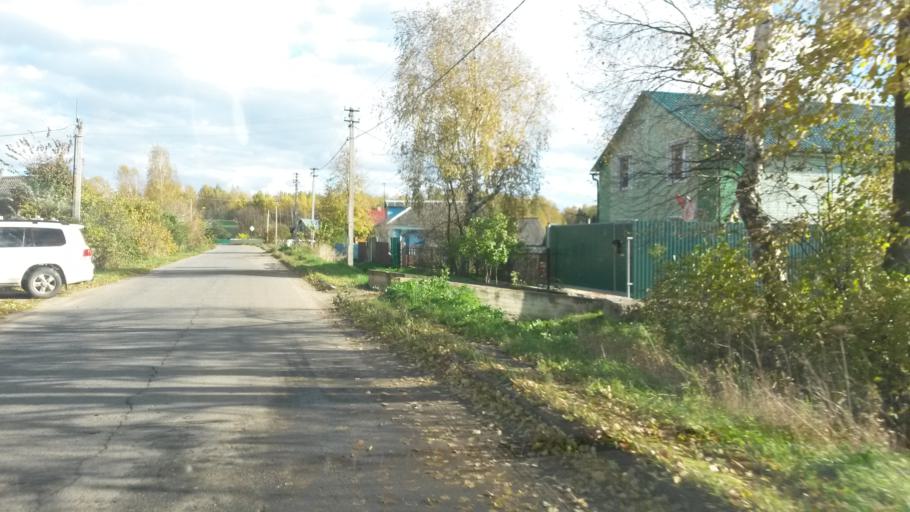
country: RU
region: Jaroslavl
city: Tunoshna
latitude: 57.5261
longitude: 39.9824
